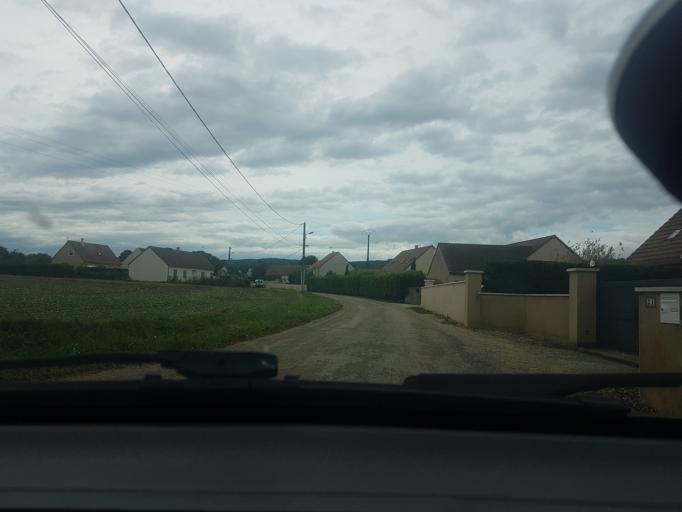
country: FR
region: Bourgogne
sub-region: Departement de Saone-et-Loire
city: Rully
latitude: 46.8759
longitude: 4.7558
